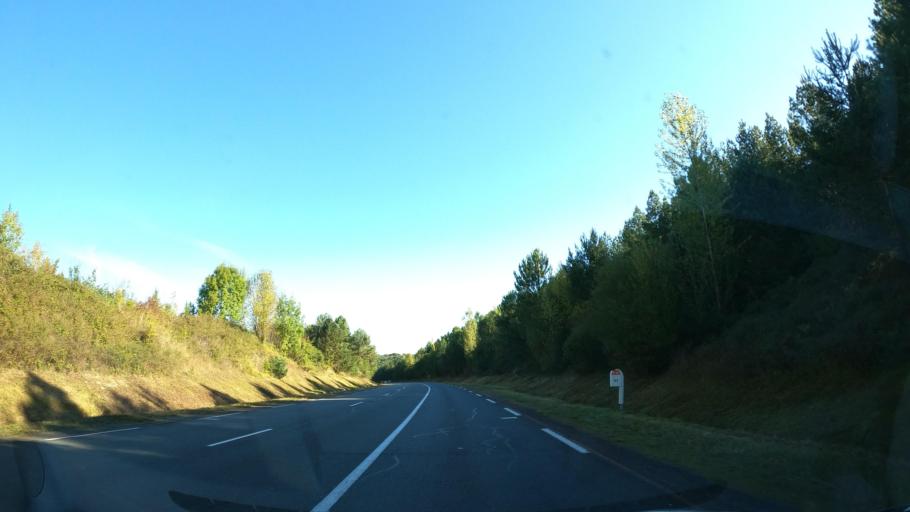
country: FR
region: Aquitaine
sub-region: Departement de la Dordogne
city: Lembras
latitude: 44.9817
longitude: 0.5984
